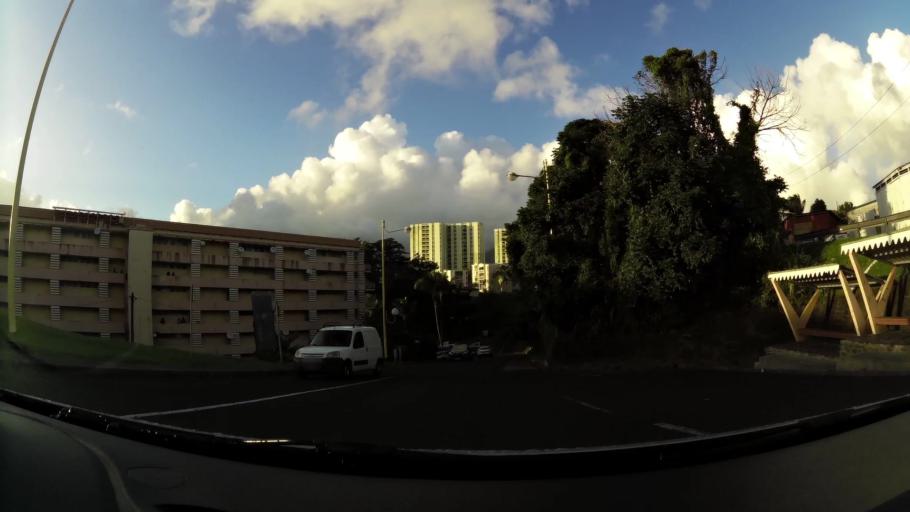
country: MQ
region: Martinique
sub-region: Martinique
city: Fort-de-France
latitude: 14.6292
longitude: -61.0695
